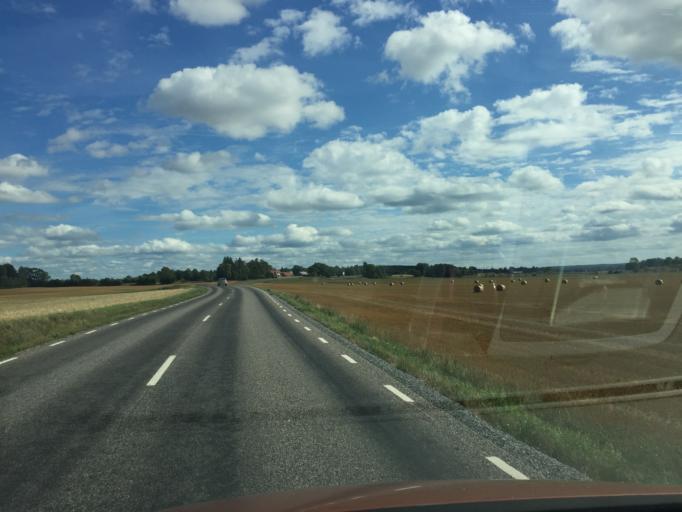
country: SE
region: OErebro
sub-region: Hallsbergs Kommun
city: Hallsberg
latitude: 59.1195
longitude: 15.0027
